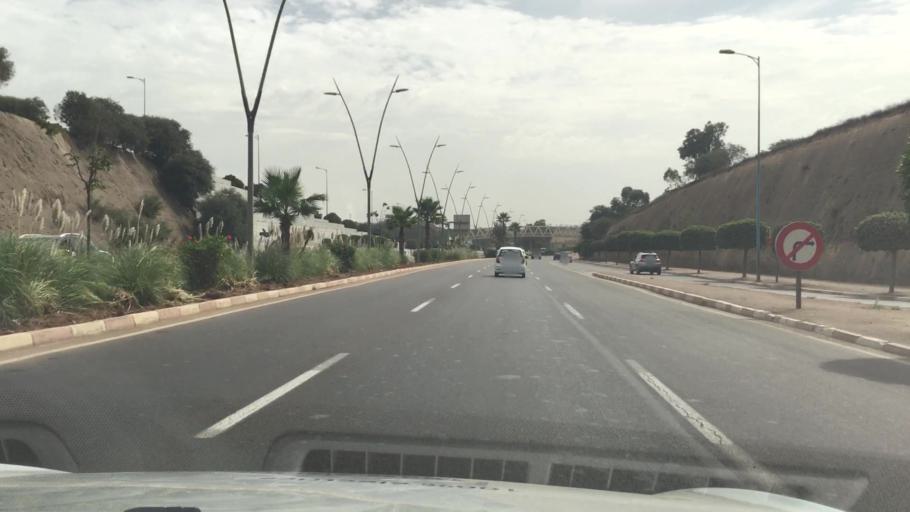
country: MA
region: Grand Casablanca
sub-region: Nouaceur
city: Bouskoura
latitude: 33.5175
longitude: -7.6323
